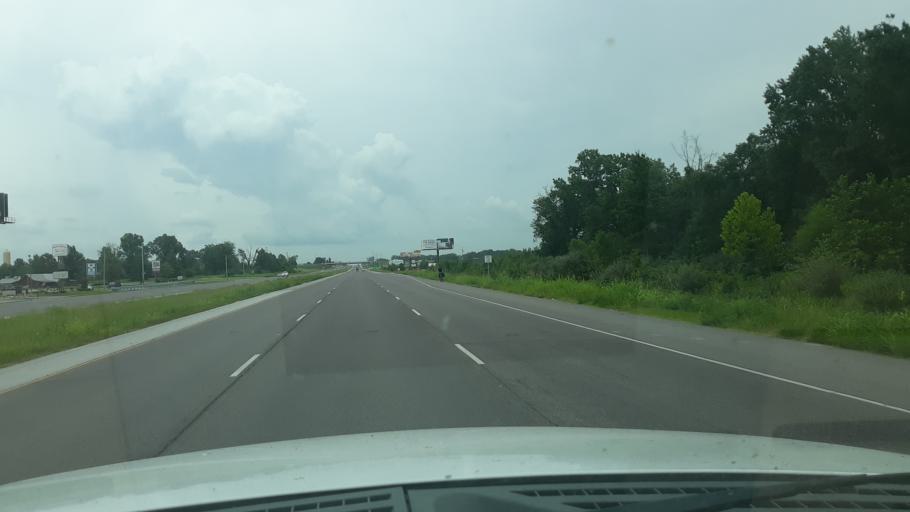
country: US
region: Illinois
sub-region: Williamson County
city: Crainville
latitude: 37.7450
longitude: -89.0709
